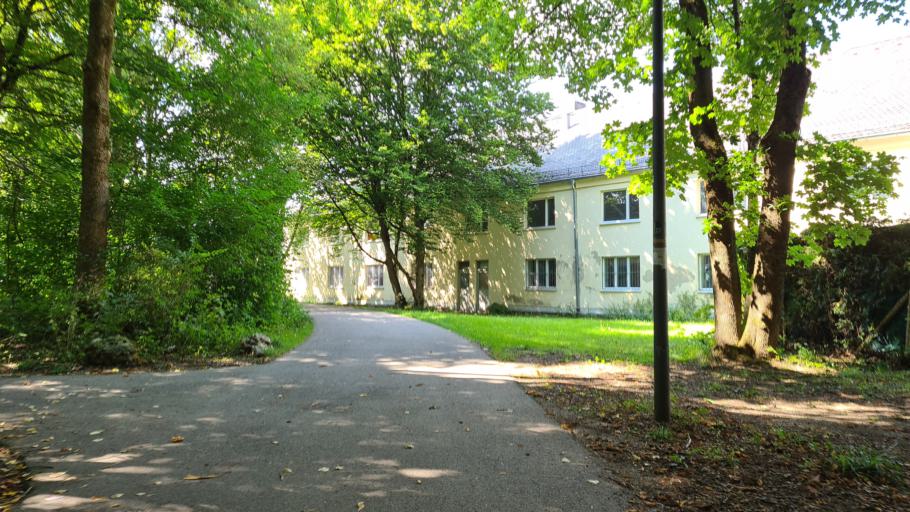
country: DE
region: Bavaria
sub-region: Upper Bavaria
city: Neuried
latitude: 48.0942
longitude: 11.4831
